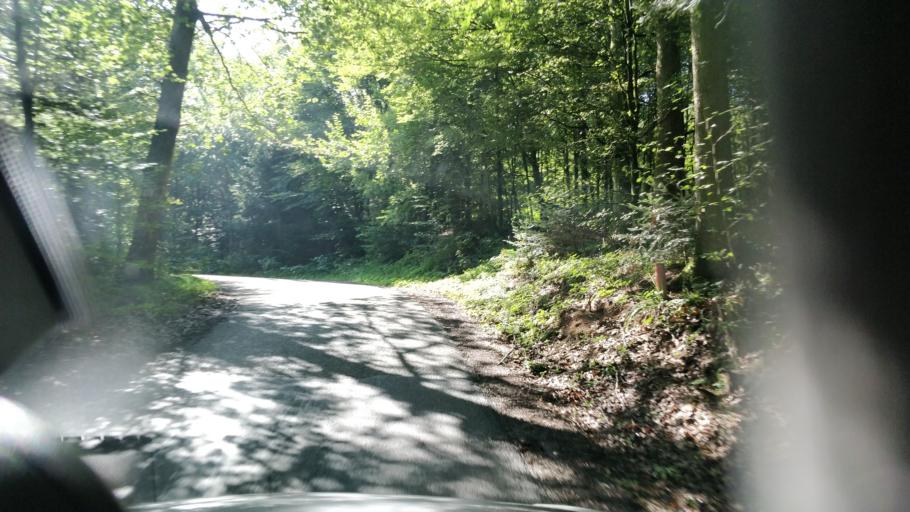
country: DE
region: Baden-Wuerttemberg
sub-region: Regierungsbezirk Stuttgart
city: Oberrot
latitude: 48.9937
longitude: 9.6574
